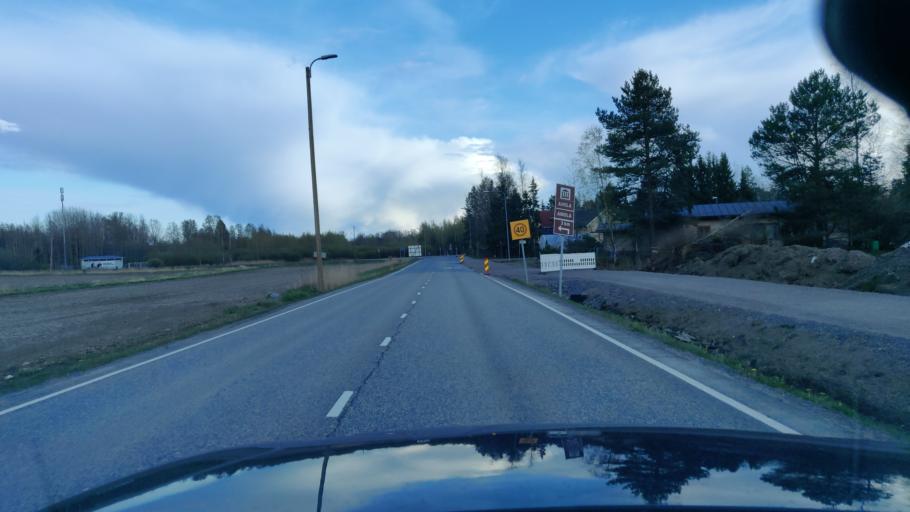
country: FI
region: Uusimaa
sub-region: Helsinki
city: Jaervenpaeae
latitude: 60.4709
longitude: 25.0698
